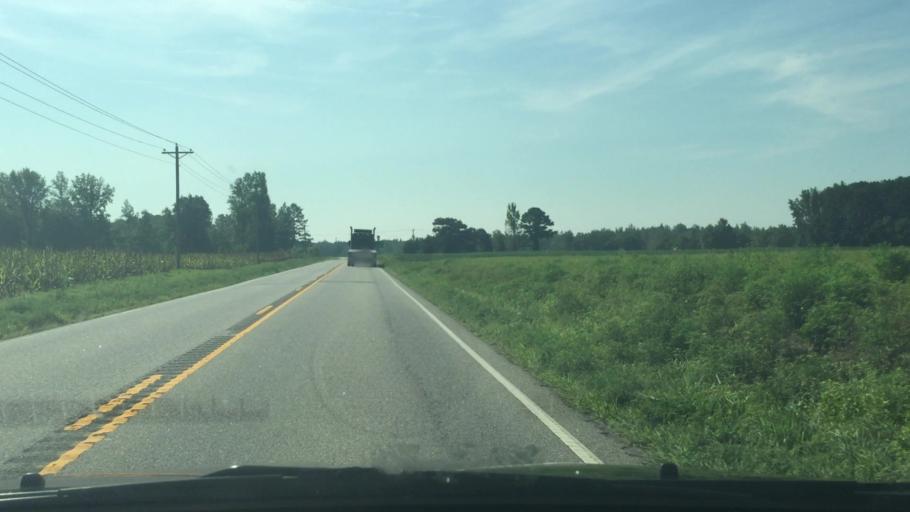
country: US
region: Virginia
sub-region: Sussex County
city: Sussex
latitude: 36.9942
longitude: -77.2588
